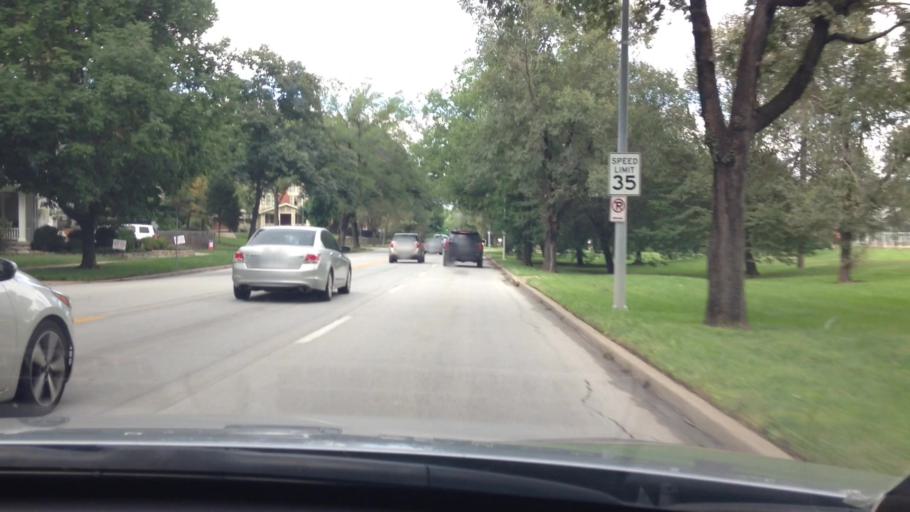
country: US
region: Kansas
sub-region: Johnson County
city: Mission Hills
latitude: 39.0247
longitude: -94.5860
